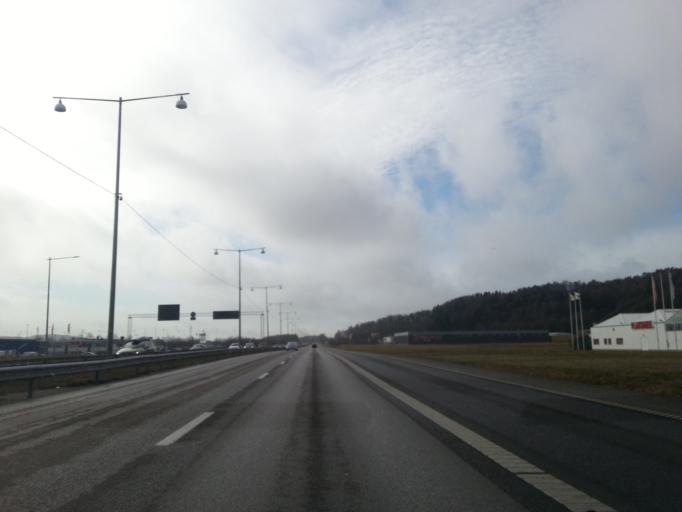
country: SE
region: Vaestra Goetaland
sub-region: Goteborg
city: Hammarkullen
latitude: 57.7729
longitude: 11.9966
